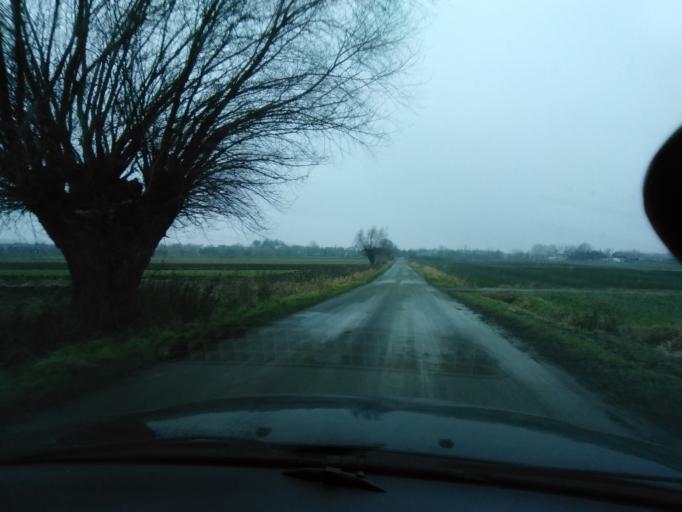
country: PL
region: Subcarpathian Voivodeship
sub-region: Powiat przeworski
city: Zarzecze
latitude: 49.9714
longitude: 22.5643
